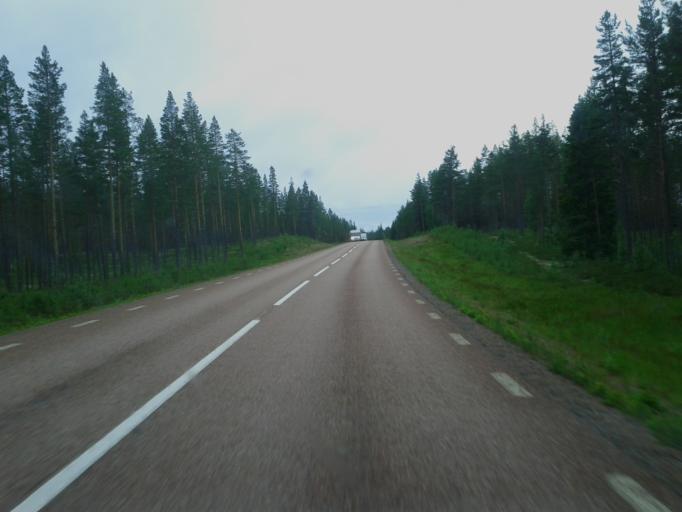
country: SE
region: Dalarna
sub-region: Alvdalens Kommun
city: AElvdalen
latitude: 61.4882
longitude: 13.4209
